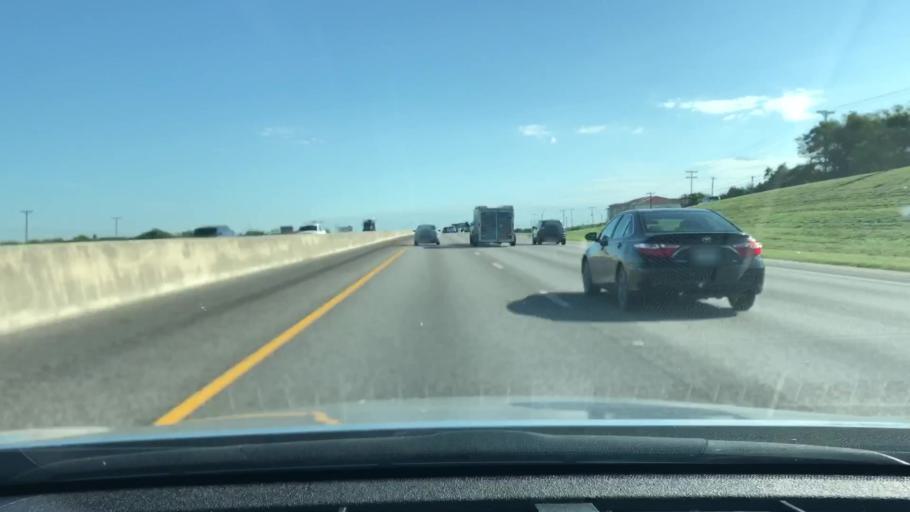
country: US
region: Texas
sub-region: Guadalupe County
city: Northcliff
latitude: 29.6522
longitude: -98.1912
